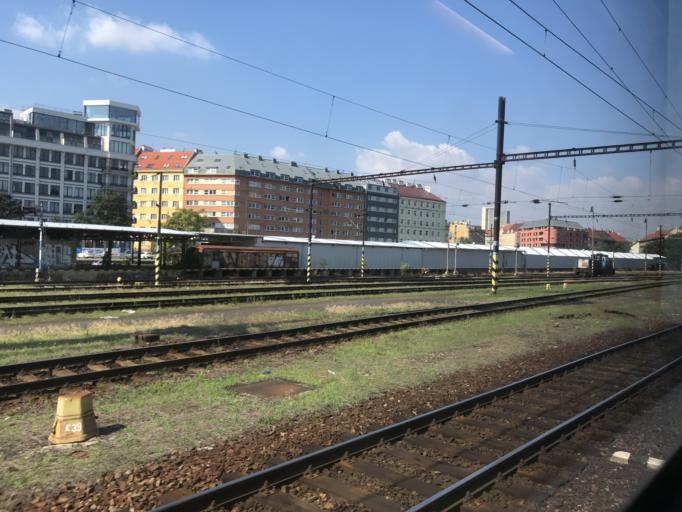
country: CZ
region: Praha
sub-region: Praha 8
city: Karlin
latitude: 50.0635
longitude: 14.4511
